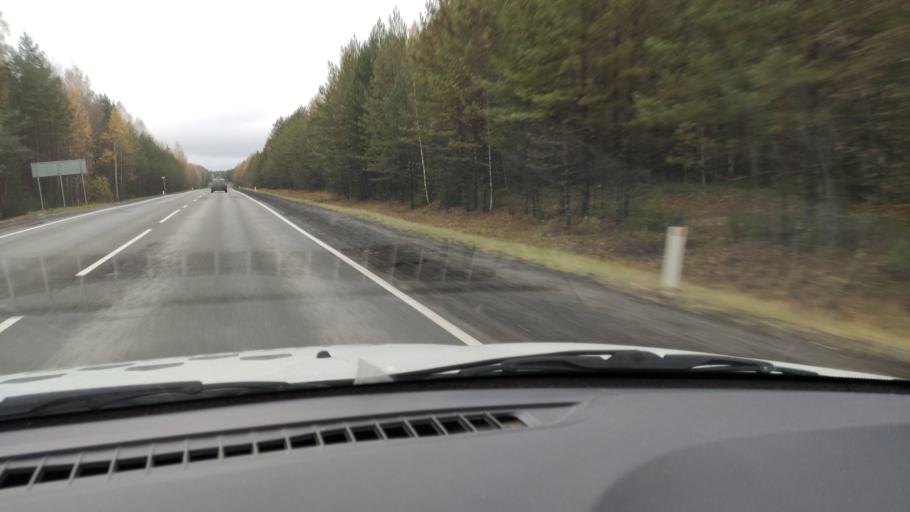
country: RU
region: Kirov
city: Belaya Kholunitsa
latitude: 58.9021
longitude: 50.9350
